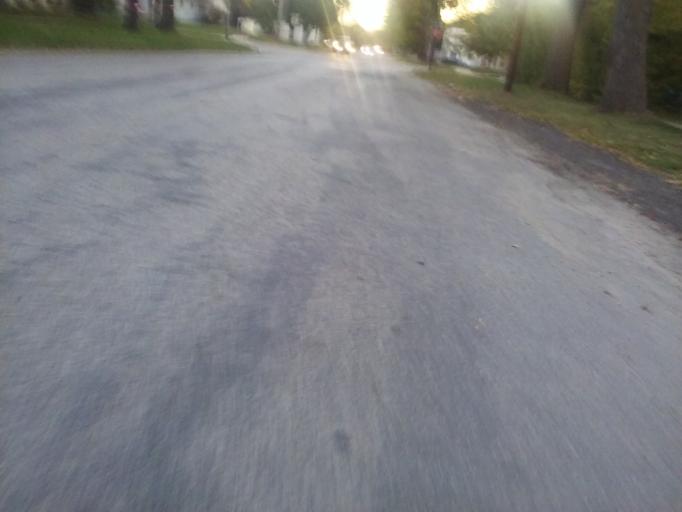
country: US
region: Iowa
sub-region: Linn County
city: Cedar Rapids
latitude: 41.9754
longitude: -91.6537
